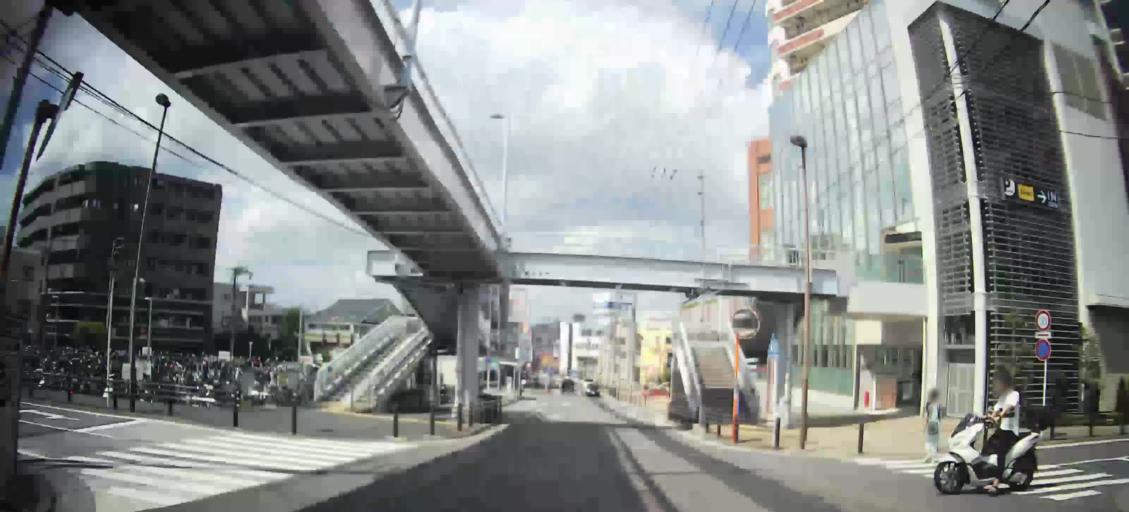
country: JP
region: Kanagawa
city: Yokohama
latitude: 35.4740
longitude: 139.5496
